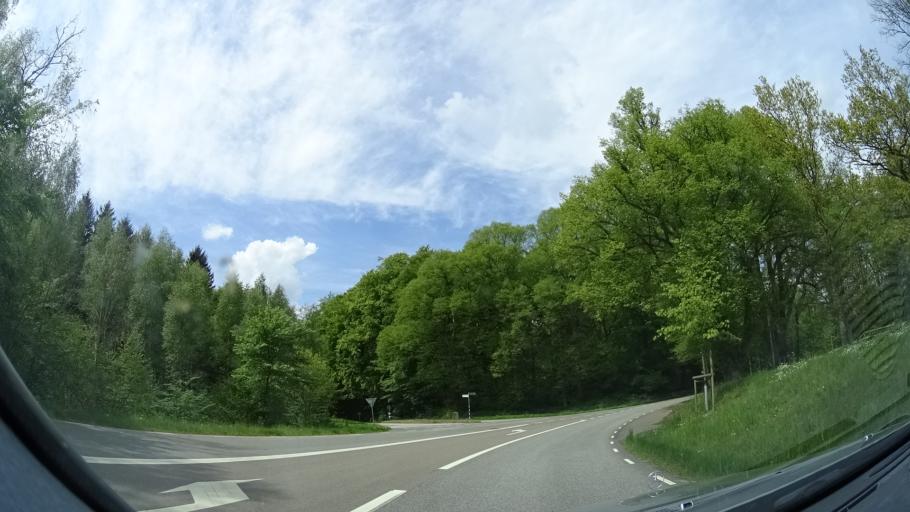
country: SE
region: Skane
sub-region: Sjobo Kommun
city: Sjoebo
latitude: 55.6822
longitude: 13.6391
